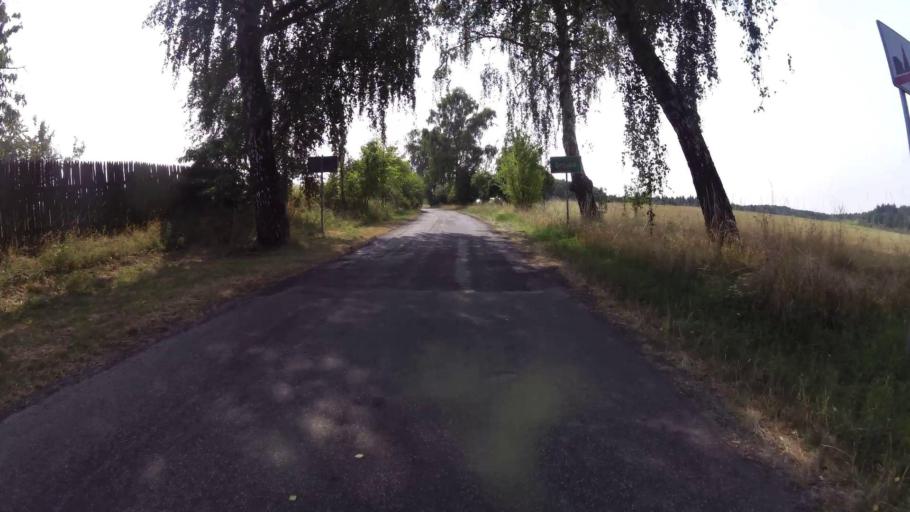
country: PL
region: West Pomeranian Voivodeship
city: Trzcinsko Zdroj
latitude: 52.9161
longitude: 14.5367
